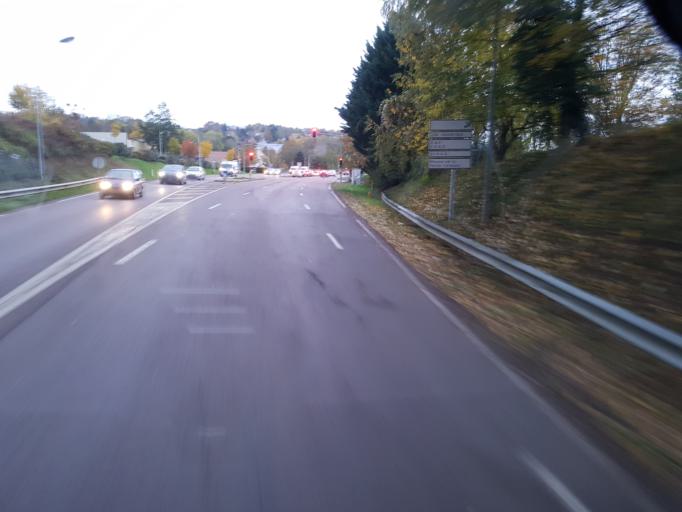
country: FR
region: Picardie
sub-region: Departement de l'Aisne
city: Chateau-Thierry
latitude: 49.0513
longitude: 3.3861
